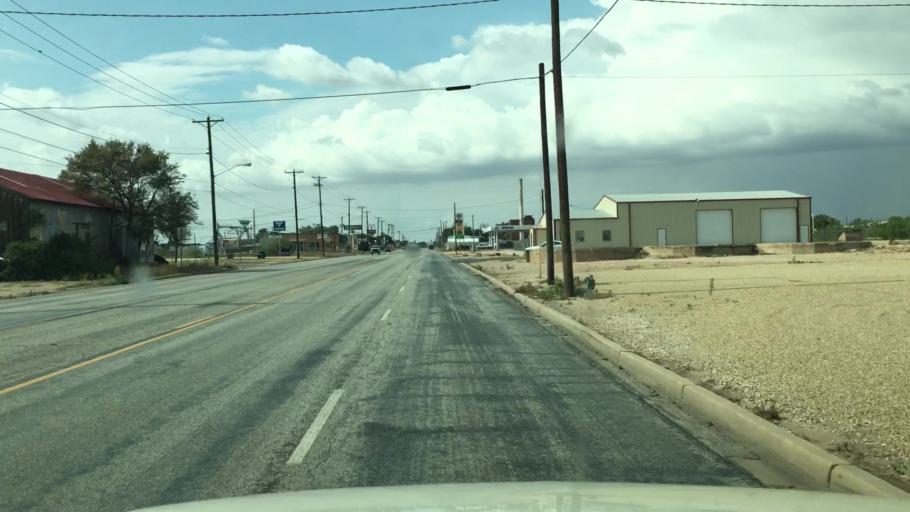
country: US
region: Texas
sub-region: Dawson County
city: Lamesa
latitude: 32.7342
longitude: -101.9494
